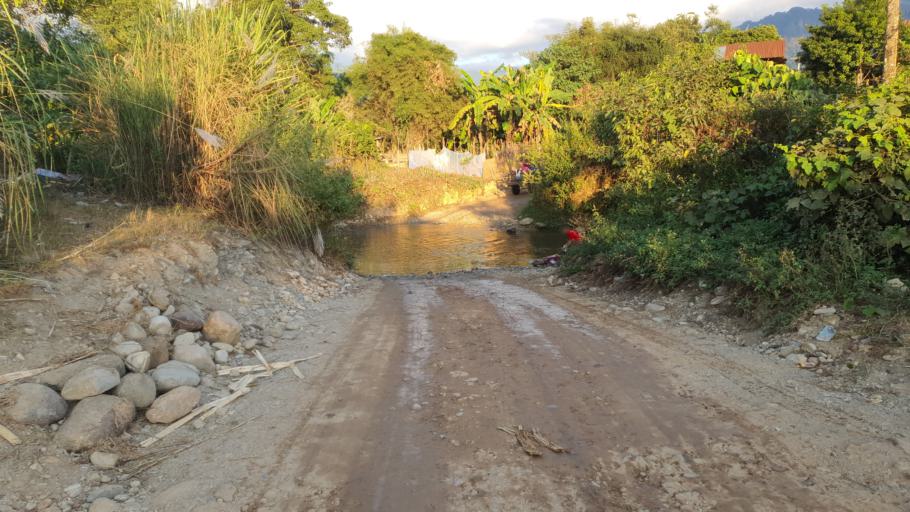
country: LA
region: Bolikhamxai
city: Bolikhan
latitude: 18.9511
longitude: 103.7891
